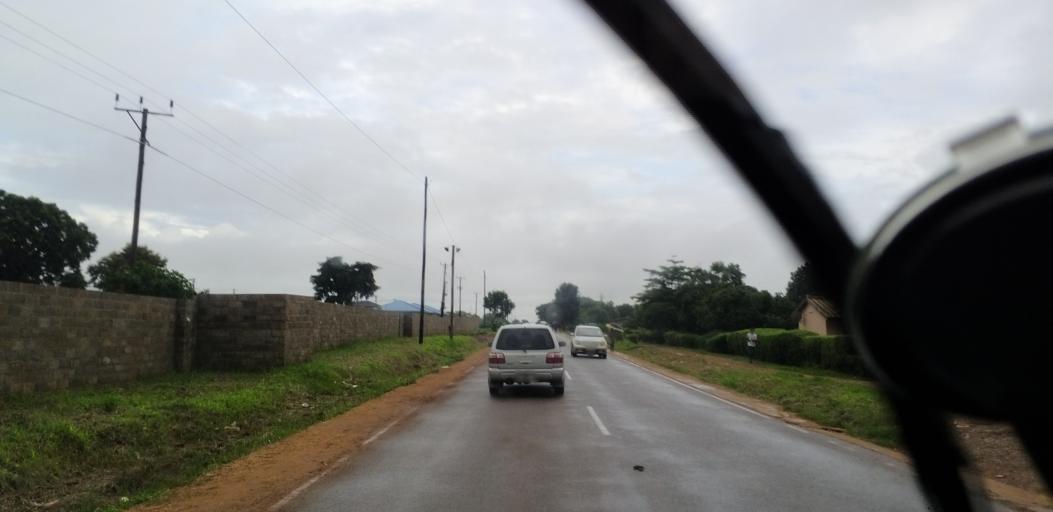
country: ZM
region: Lusaka
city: Lusaka
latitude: -15.5132
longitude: 28.3027
